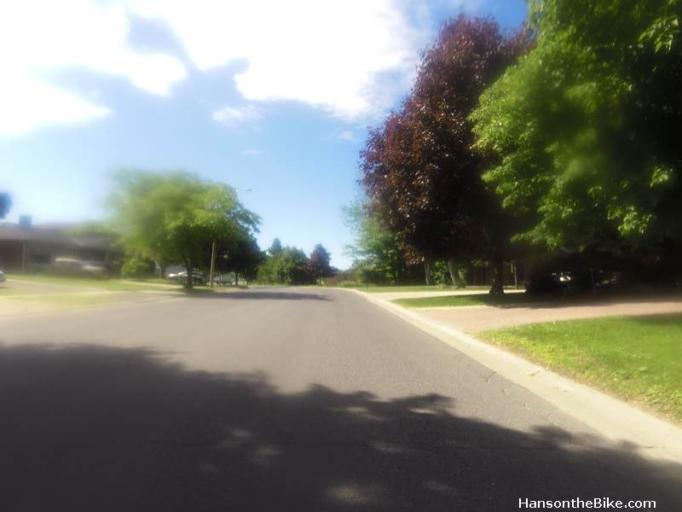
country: CA
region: Ontario
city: Kingston
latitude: 44.2244
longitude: -76.5311
